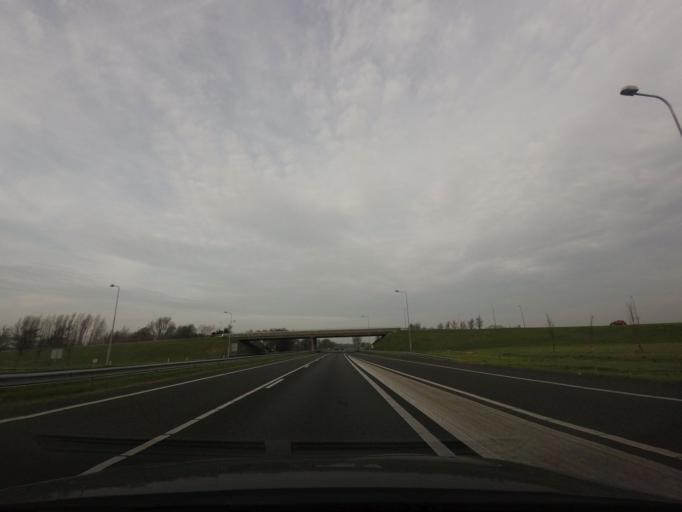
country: NL
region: North Holland
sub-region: Gemeente Medemblik
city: Opperdoes
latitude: 52.7208
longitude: 5.0253
